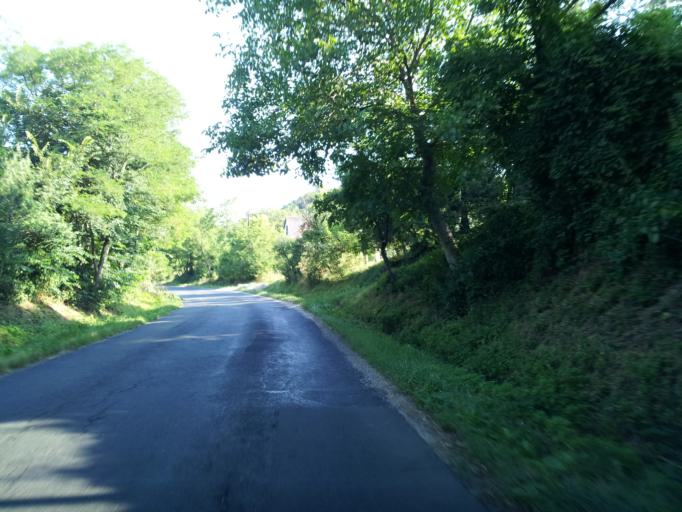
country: HU
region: Zala
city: Gyenesdias
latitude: 46.8543
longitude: 17.3416
